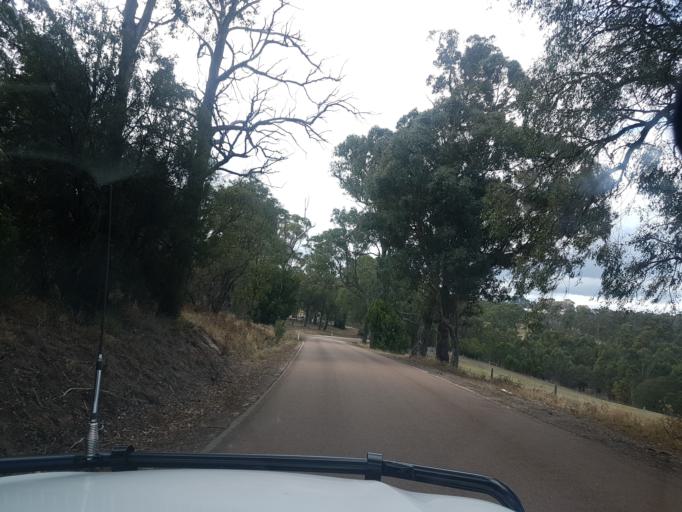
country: AU
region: Victoria
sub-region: East Gippsland
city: Bairnsdale
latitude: -37.7880
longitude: 147.5867
